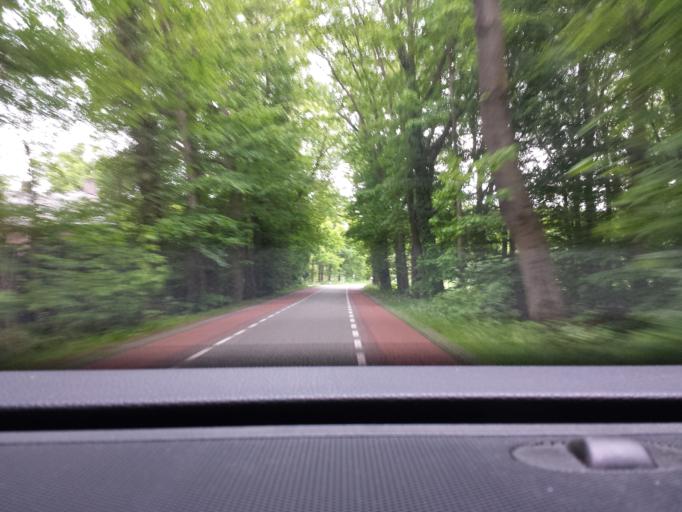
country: NL
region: Gelderland
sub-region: Gemeente Lochem
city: Lochem
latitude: 52.1245
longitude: 6.3848
